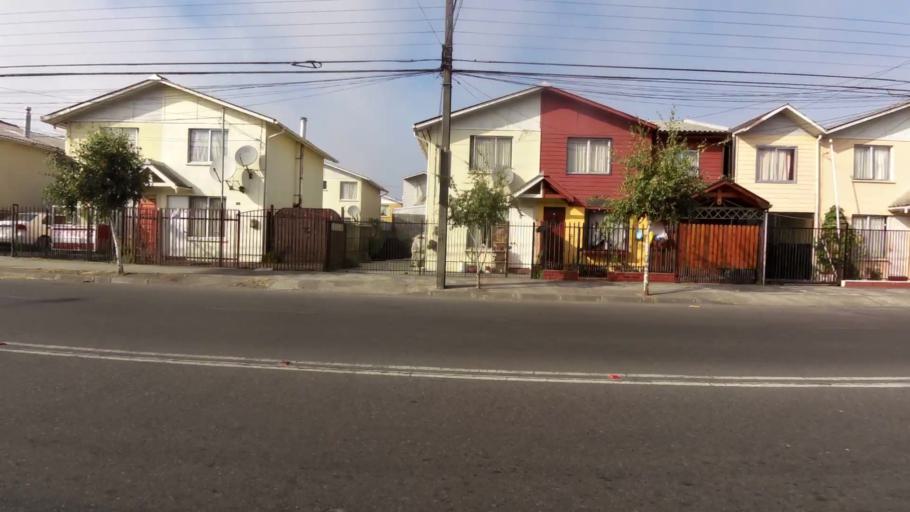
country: CL
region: Biobio
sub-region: Provincia de Concepcion
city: Concepcion
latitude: -36.7980
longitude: -73.1113
